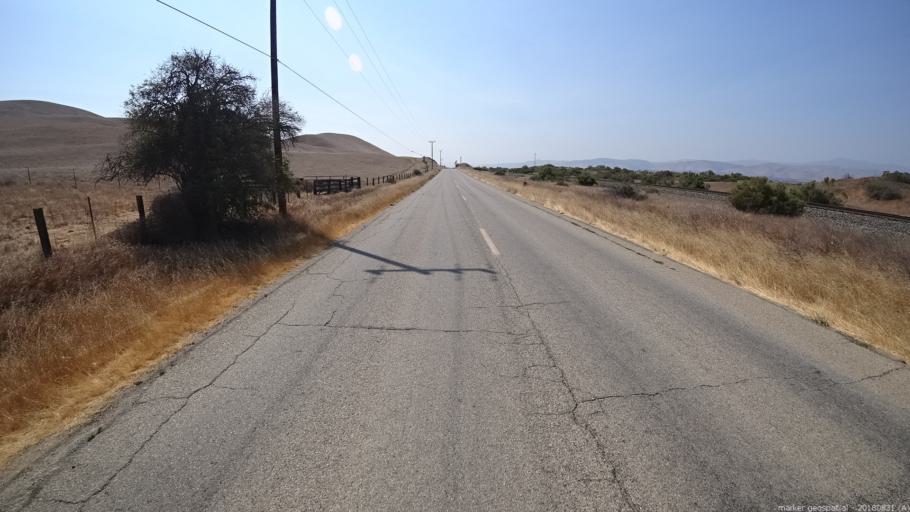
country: US
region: California
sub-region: Monterey County
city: Greenfield
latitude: 36.3443
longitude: -121.2007
